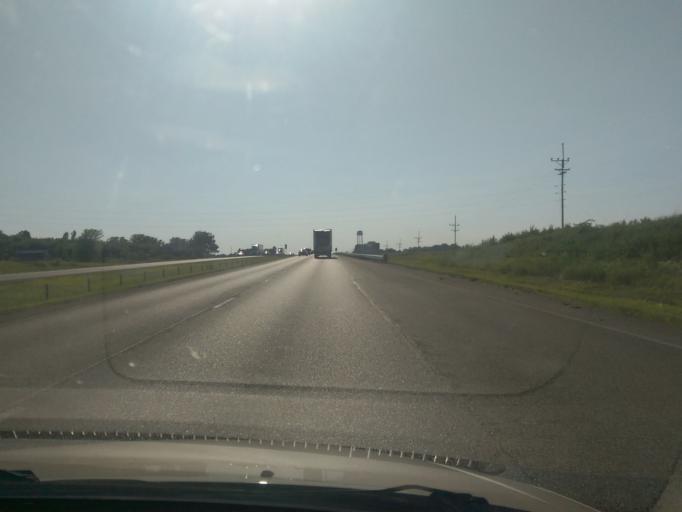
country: US
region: Missouri
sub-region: Lafayette County
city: Higginsville
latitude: 39.0029
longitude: -93.8136
